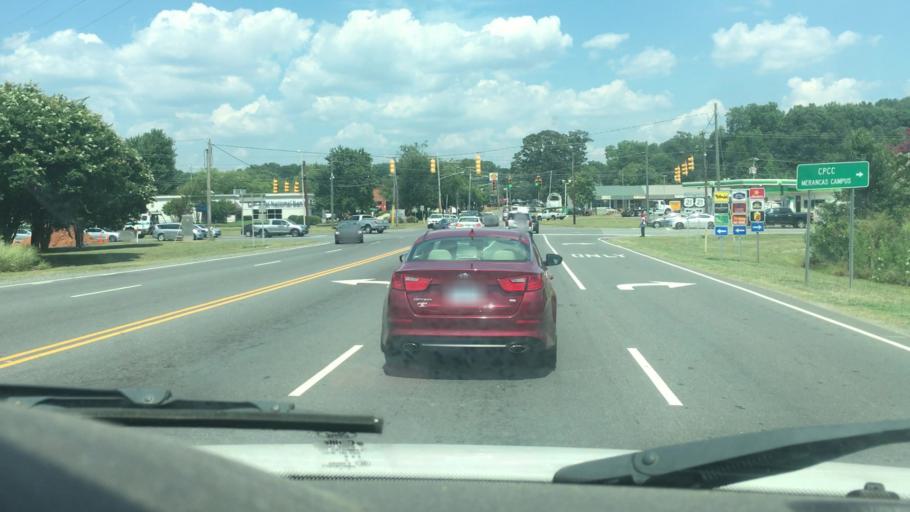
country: US
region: North Carolina
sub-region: Mecklenburg County
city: Huntersville
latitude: 35.4096
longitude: -80.8558
